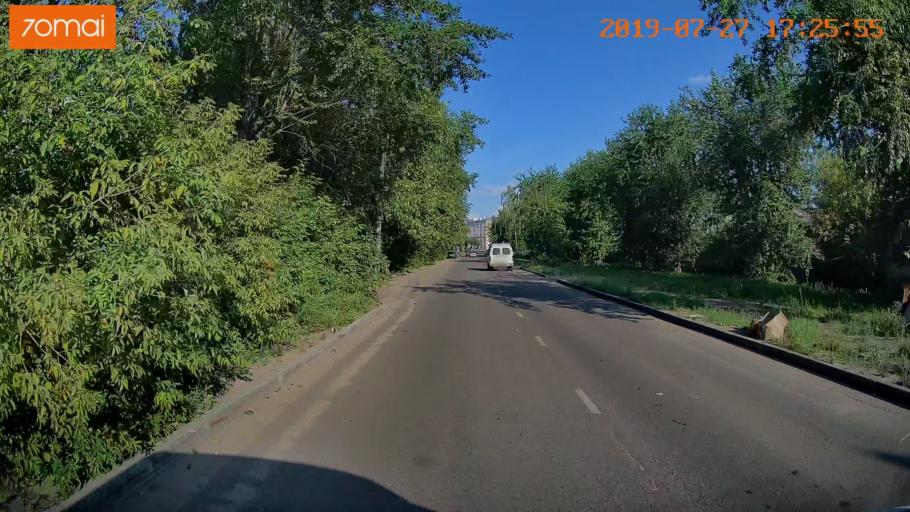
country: RU
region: Ivanovo
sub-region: Gorod Ivanovo
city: Ivanovo
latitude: 57.0157
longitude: 40.9661
